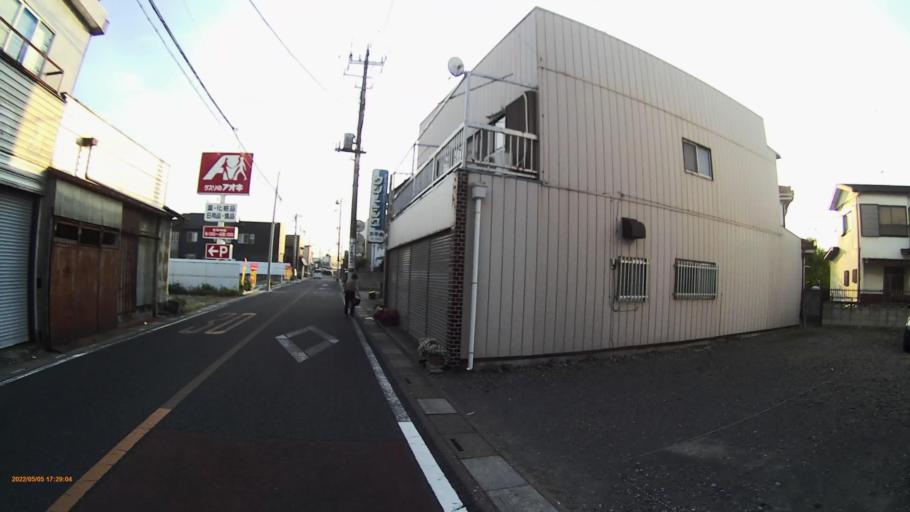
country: JP
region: Saitama
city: Kurihashi
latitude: 36.1390
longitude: 139.6979
